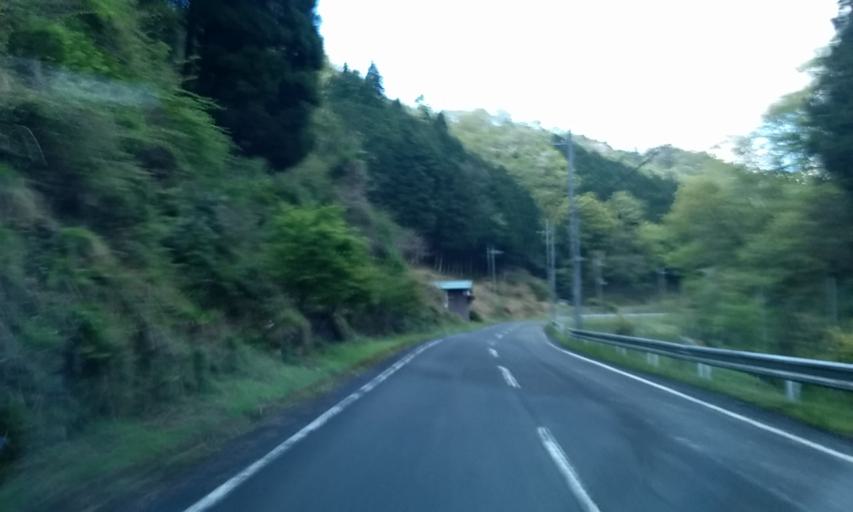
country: JP
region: Kyoto
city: Ayabe
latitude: 35.2551
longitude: 135.3138
